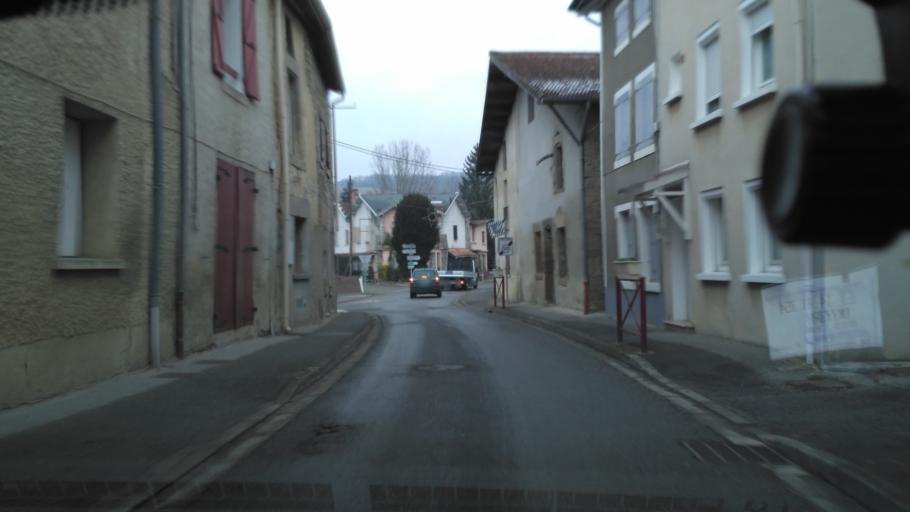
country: FR
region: Rhone-Alpes
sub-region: Departement de la Drome
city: Genissieux
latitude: 45.1458
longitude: 5.1227
